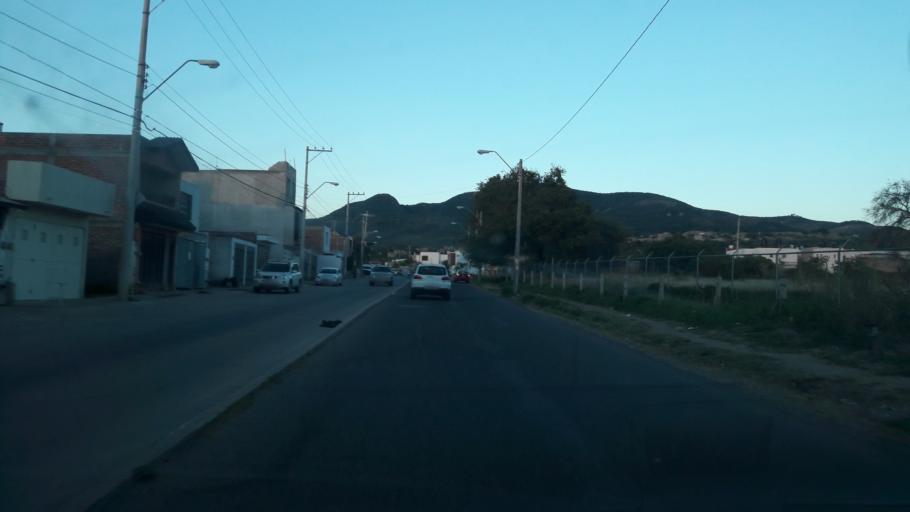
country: MX
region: Guanajuato
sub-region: Leon
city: Medina
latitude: 21.1597
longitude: -101.6343
